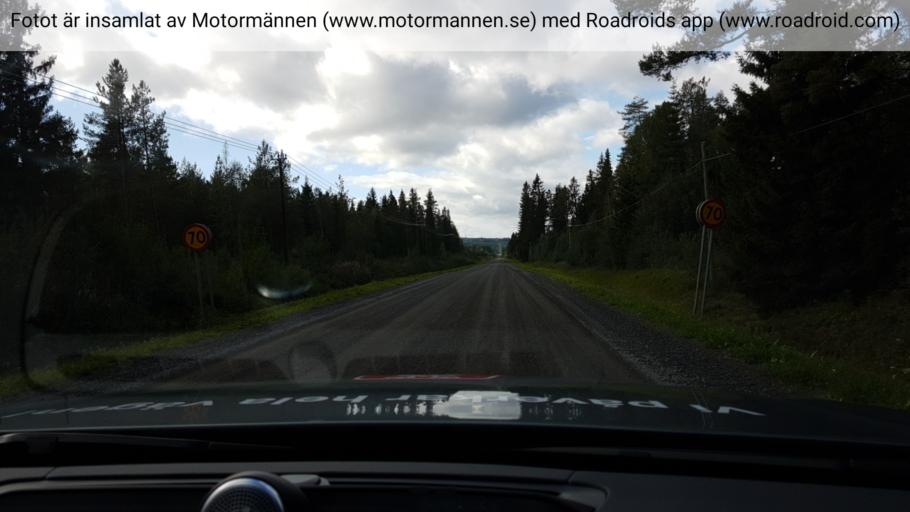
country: SE
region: Jaemtland
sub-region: Stroemsunds Kommun
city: Stroemsund
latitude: 63.6250
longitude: 15.1950
